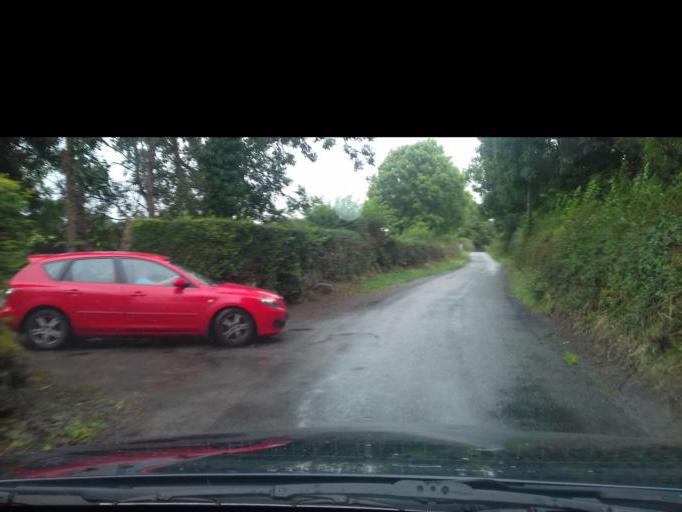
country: IE
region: Leinster
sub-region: Kilkenny
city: Graiguenamanagh
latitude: 52.5816
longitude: -6.9393
